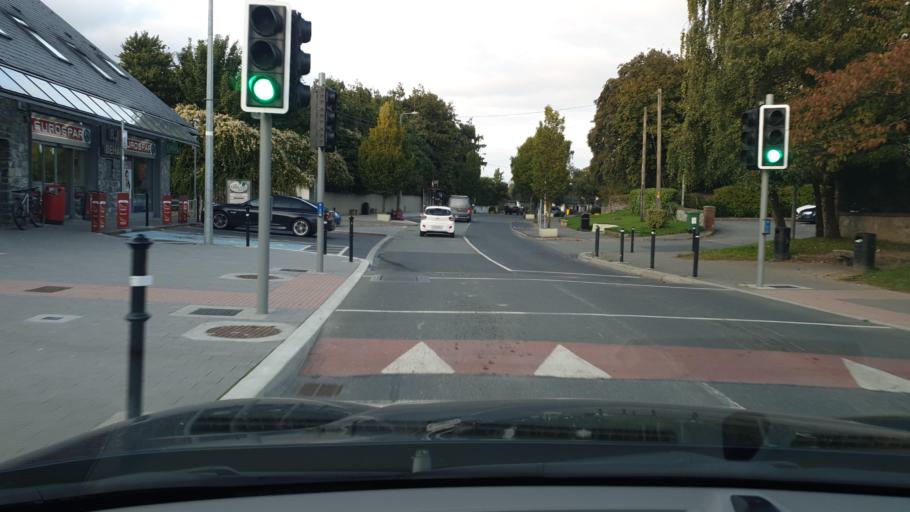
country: IE
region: Leinster
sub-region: Kildare
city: Kill
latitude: 53.2476
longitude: -6.5925
